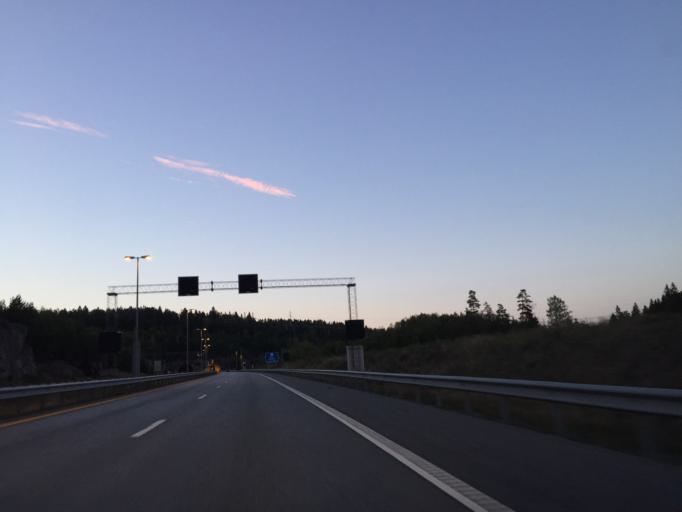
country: NO
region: Akershus
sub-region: Vestby
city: Vestby
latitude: 59.5234
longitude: 10.7291
